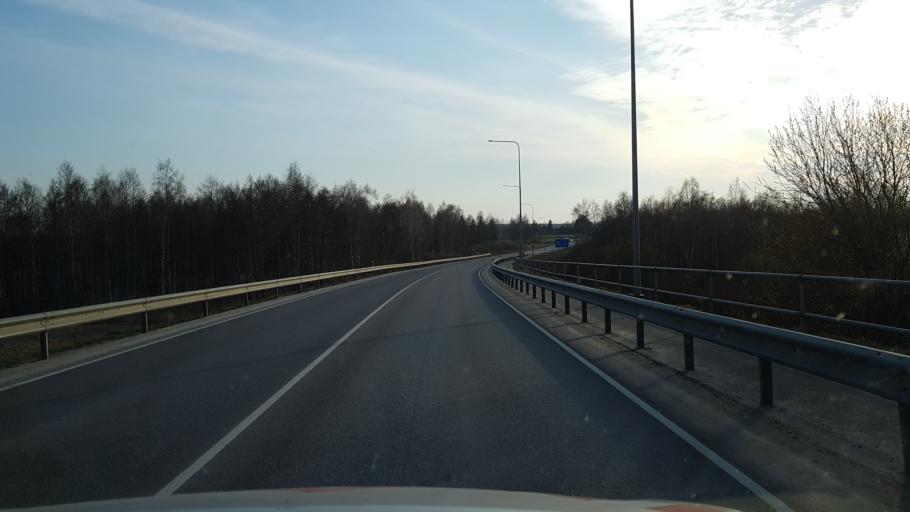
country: EE
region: Laeaene-Virumaa
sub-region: Someru vald
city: Someru
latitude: 59.3576
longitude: 26.4049
